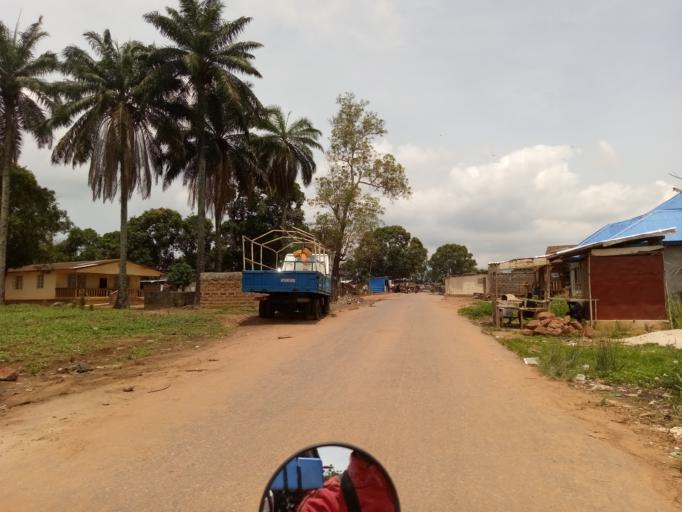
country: SL
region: Western Area
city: Waterloo
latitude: 8.3321
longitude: -13.0426
